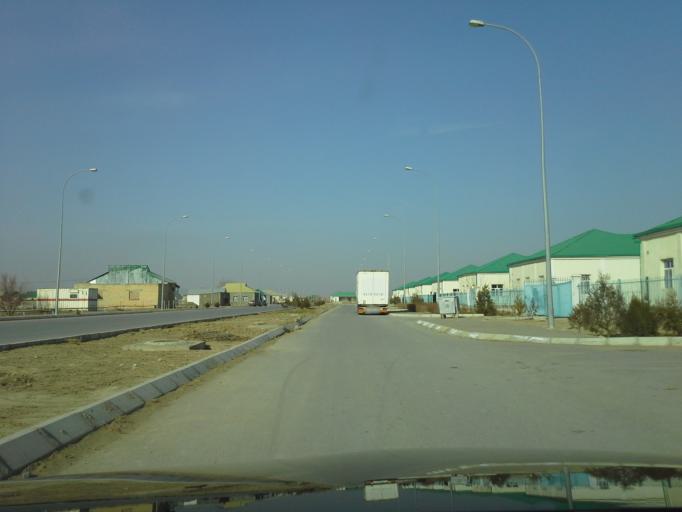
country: TM
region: Ahal
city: Abadan
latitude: 38.1729
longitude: 58.0473
